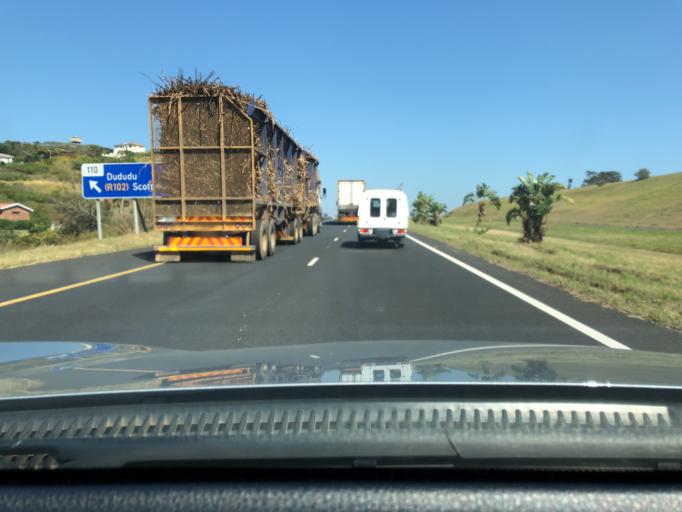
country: ZA
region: KwaZulu-Natal
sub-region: Ugu District Municipality
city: Scottburgh
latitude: -30.2648
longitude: 30.7580
